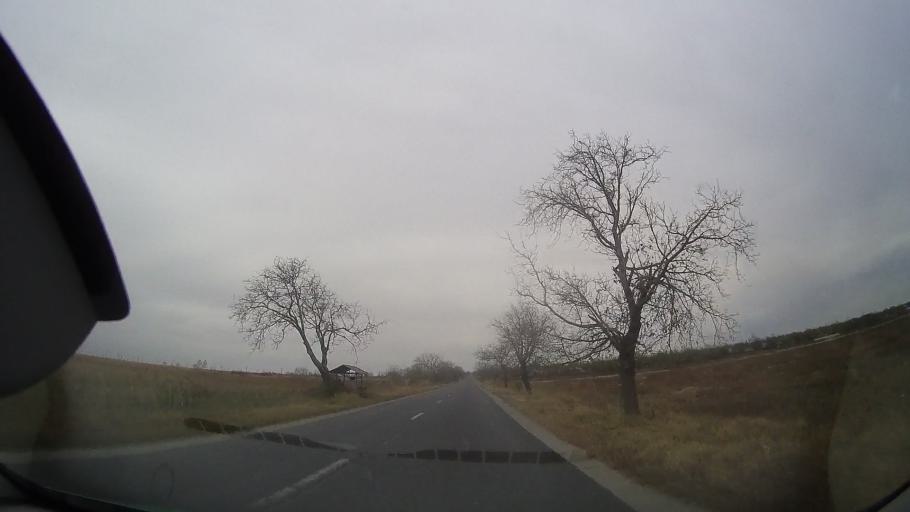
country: RO
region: Braila
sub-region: Comuna Ciocile
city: Ciocile
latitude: 44.7758
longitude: 27.1704
